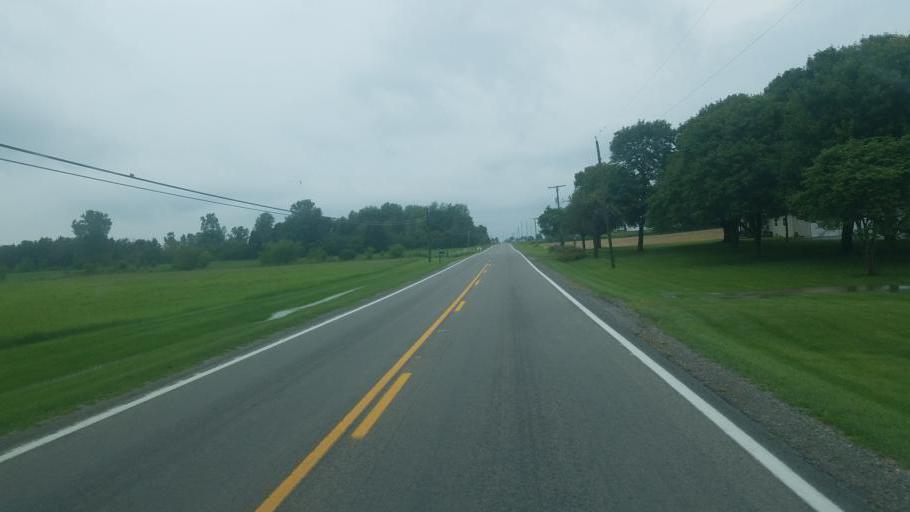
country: US
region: Ohio
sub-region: Hardin County
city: Kenton
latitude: 40.6050
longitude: -83.7120
